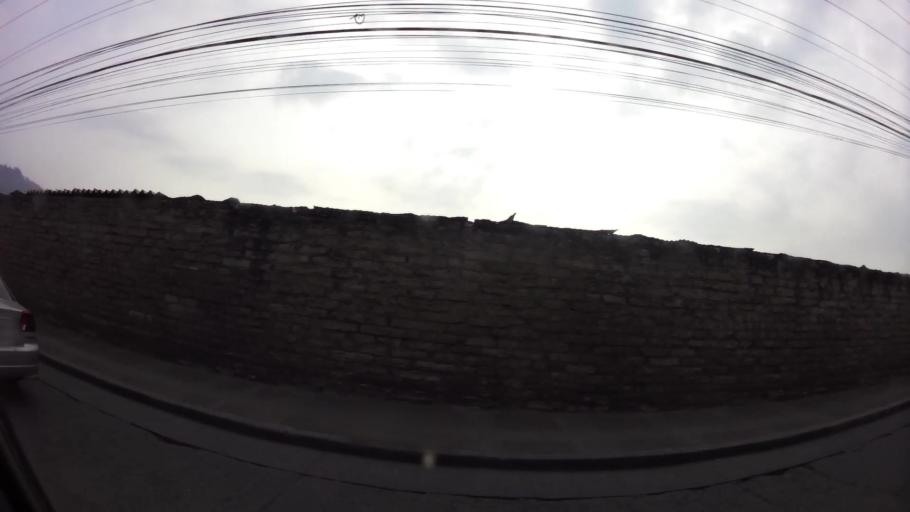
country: HN
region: Francisco Morazan
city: Tegucigalpa
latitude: 14.0957
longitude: -87.1986
